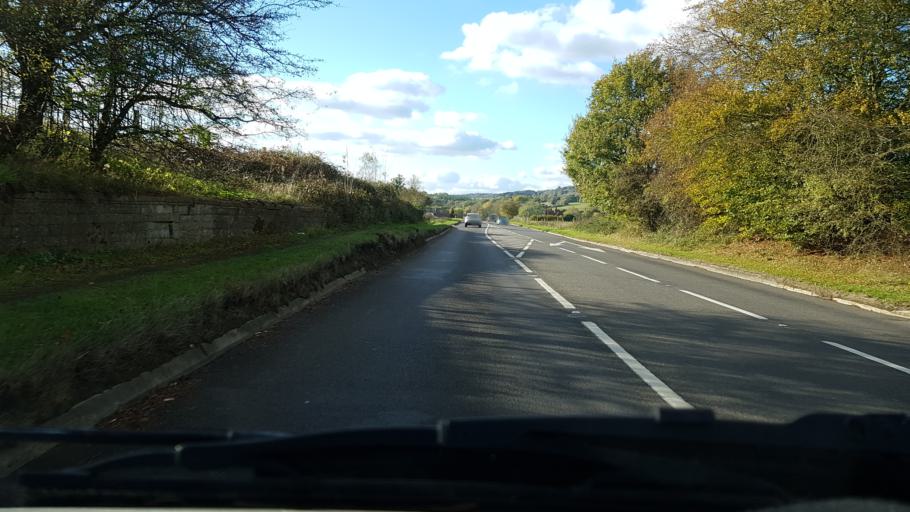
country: GB
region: England
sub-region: Surrey
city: Chilworth
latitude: 51.2232
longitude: -0.4731
